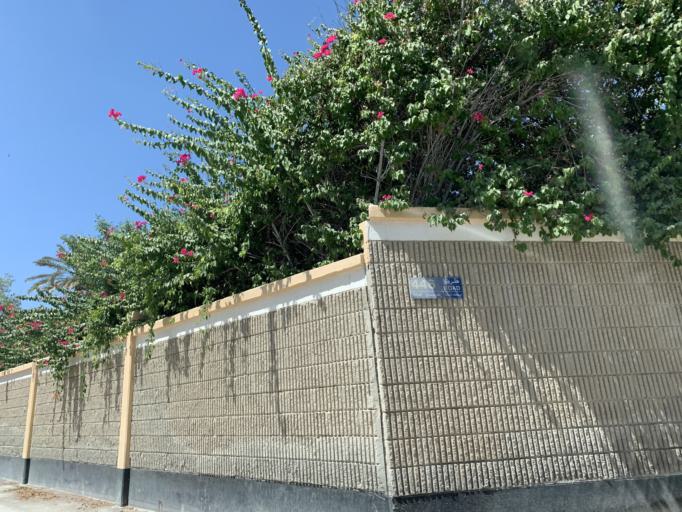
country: BH
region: Manama
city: Jidd Hafs
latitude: 26.2216
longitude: 50.4951
